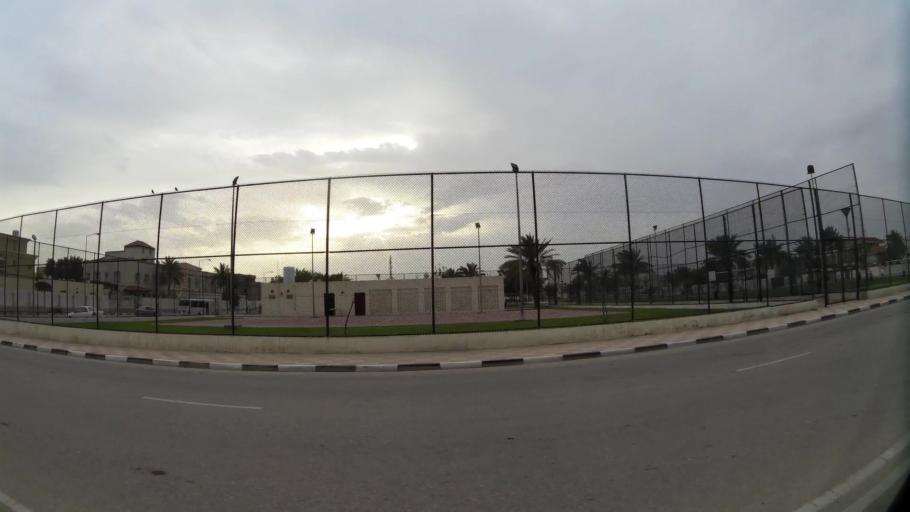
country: QA
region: Baladiyat ad Dawhah
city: Doha
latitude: 25.3288
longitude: 51.5107
